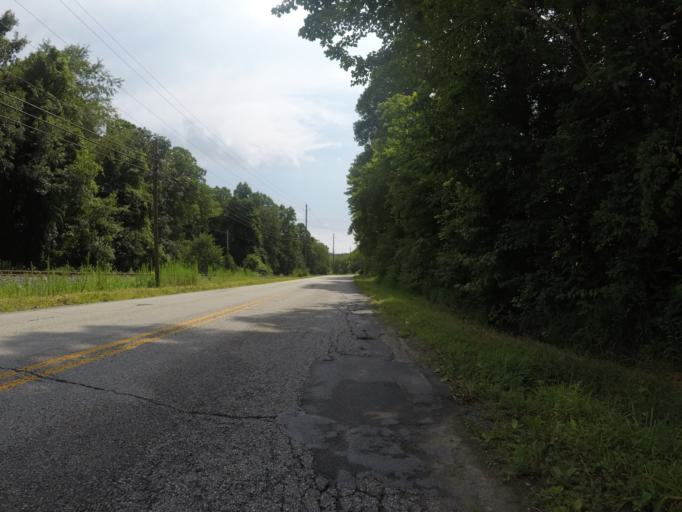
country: US
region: Kentucky
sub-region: Boyd County
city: Ironville
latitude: 38.4458
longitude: -82.6963
